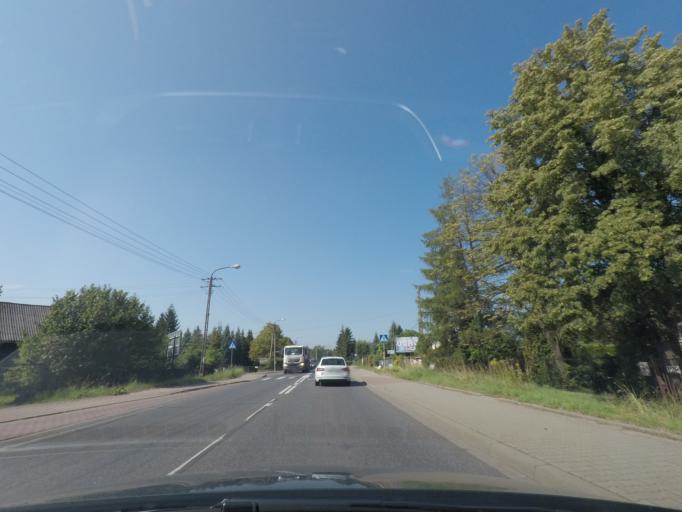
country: PL
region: Lesser Poland Voivodeship
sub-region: Powiat chrzanowski
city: Chrzanow
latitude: 50.1336
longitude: 19.3816
